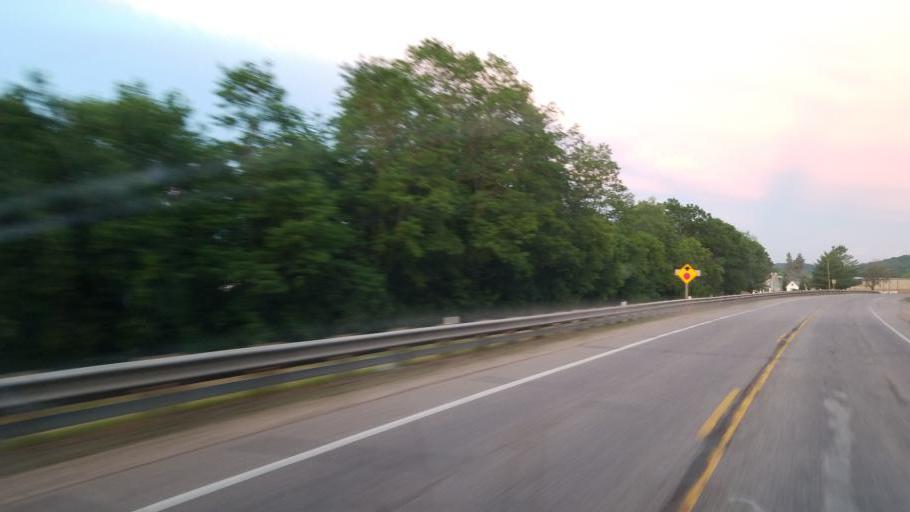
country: US
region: Wisconsin
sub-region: Juneau County
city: Elroy
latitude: 43.7442
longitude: -90.2755
